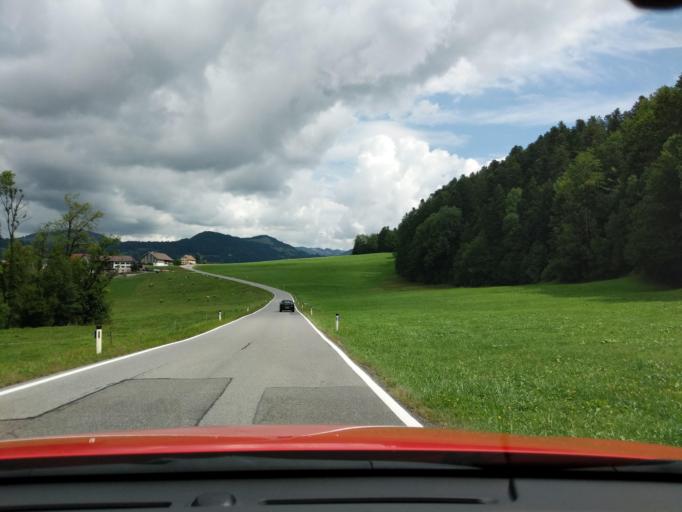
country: AT
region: Vorarlberg
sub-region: Politischer Bezirk Bregenz
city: Riefensberg
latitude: 47.5075
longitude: 9.9489
